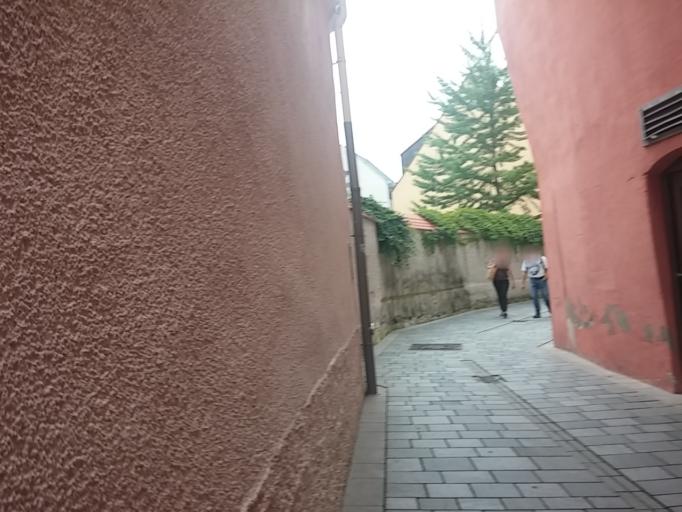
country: DE
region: Bavaria
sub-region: Swabia
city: Memmingen
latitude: 47.9861
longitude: 10.1822
